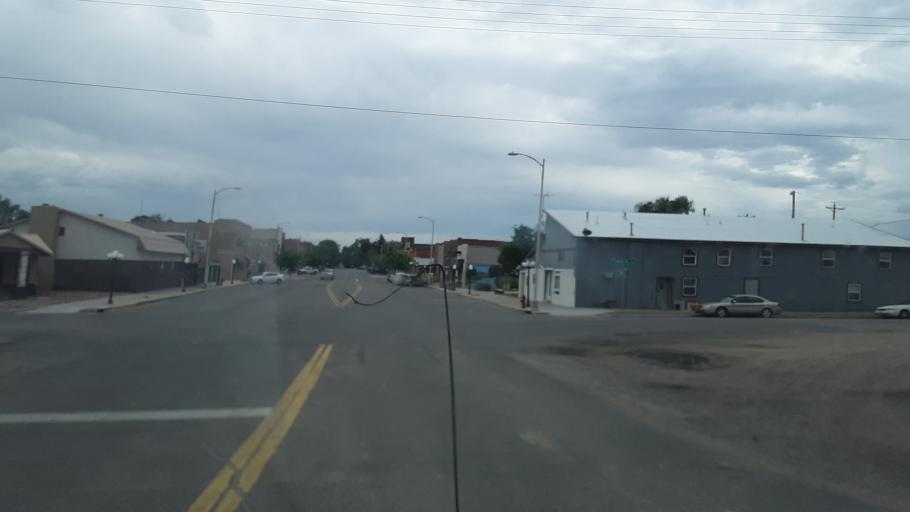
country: US
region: Colorado
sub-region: Otero County
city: Fowler
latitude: 38.1322
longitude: -104.0234
